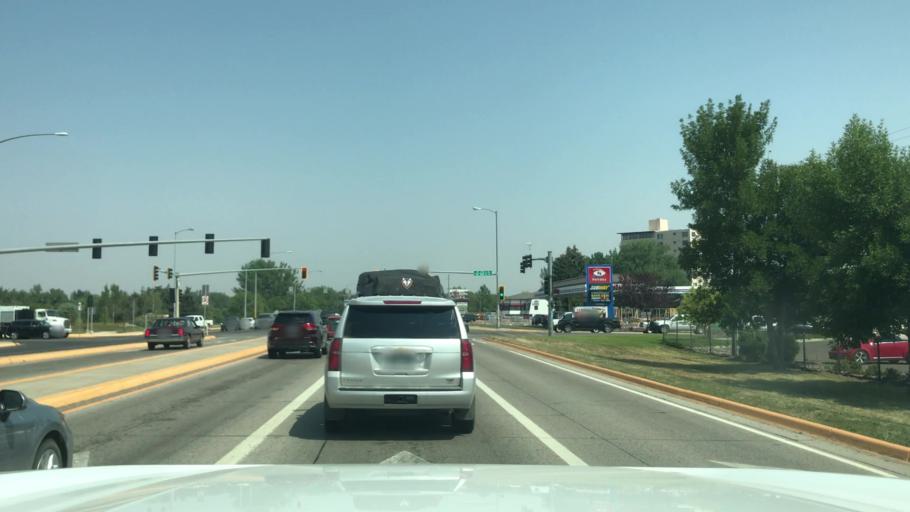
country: US
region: Montana
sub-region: Cascade County
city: Great Falls
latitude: 47.4897
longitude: -111.3297
